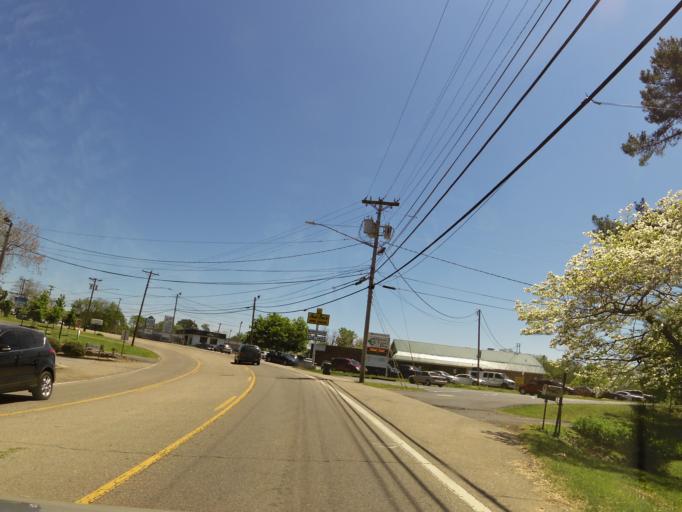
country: US
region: Tennessee
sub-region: Greene County
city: Greeneville
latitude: 36.1684
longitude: -82.8130
